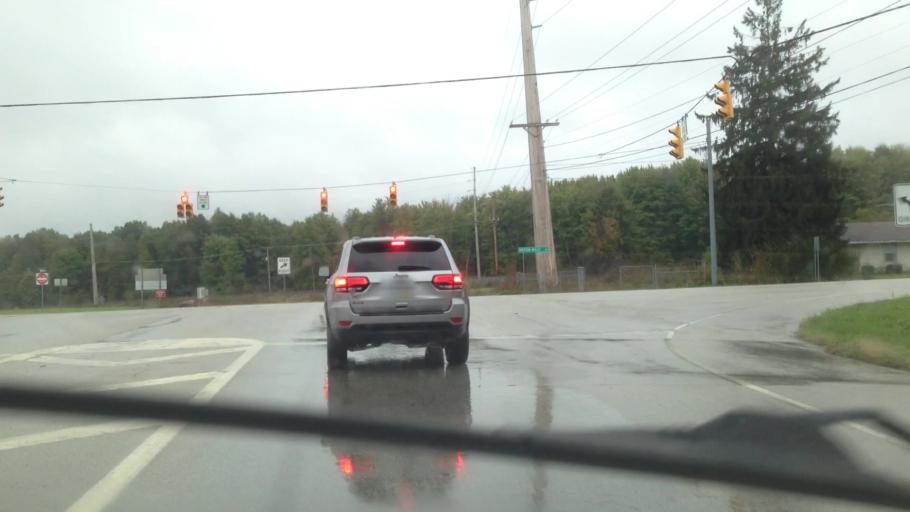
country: US
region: Ohio
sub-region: Summit County
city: Boston Heights
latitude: 41.2552
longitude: -81.5025
